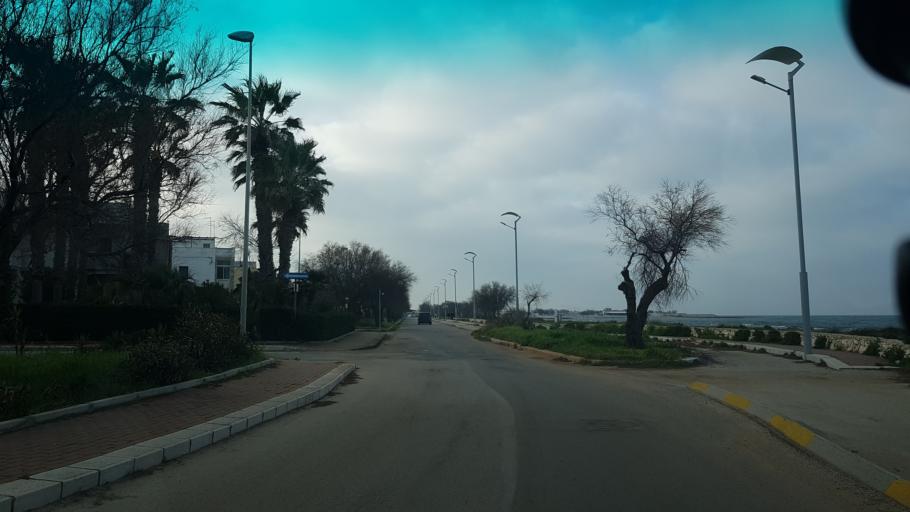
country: IT
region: Apulia
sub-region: Provincia di Brindisi
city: Carovigno
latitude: 40.7393
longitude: 17.7404
